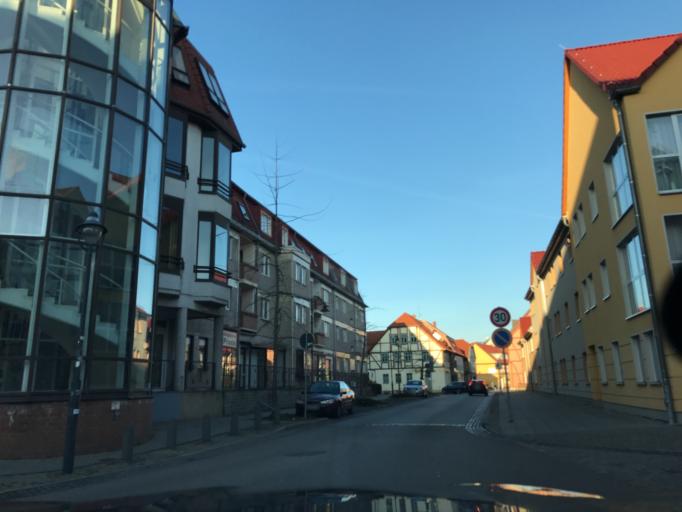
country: DE
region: Saxony-Anhalt
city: Burg bei Magdeburg
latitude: 52.2705
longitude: 11.8591
